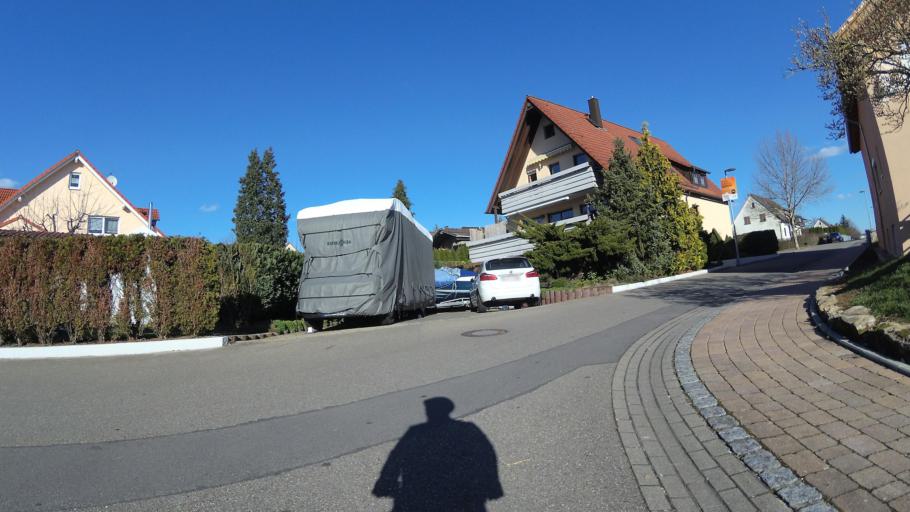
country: DE
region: Baden-Wuerttemberg
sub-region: Regierungsbezirk Stuttgart
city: Untereisesheim
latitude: 49.2335
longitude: 9.2116
